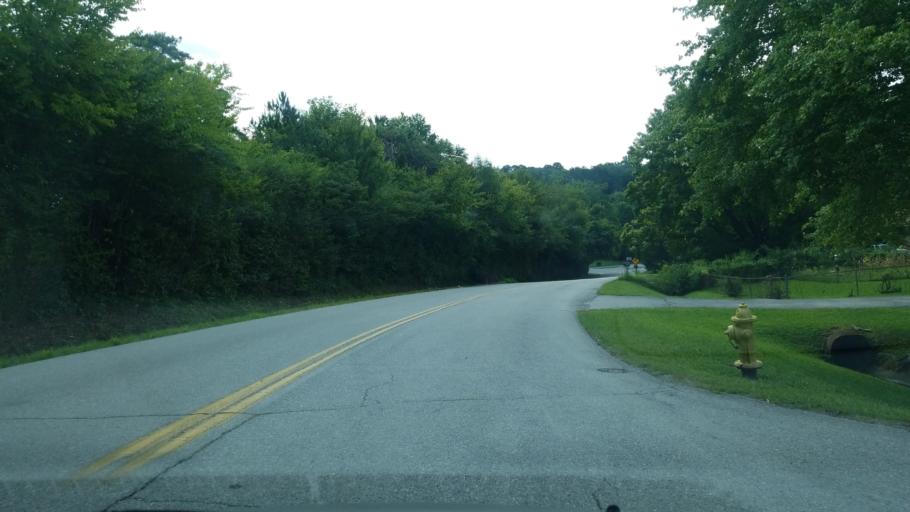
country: US
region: Tennessee
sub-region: Hamilton County
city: East Chattanooga
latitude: 35.0932
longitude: -85.2139
